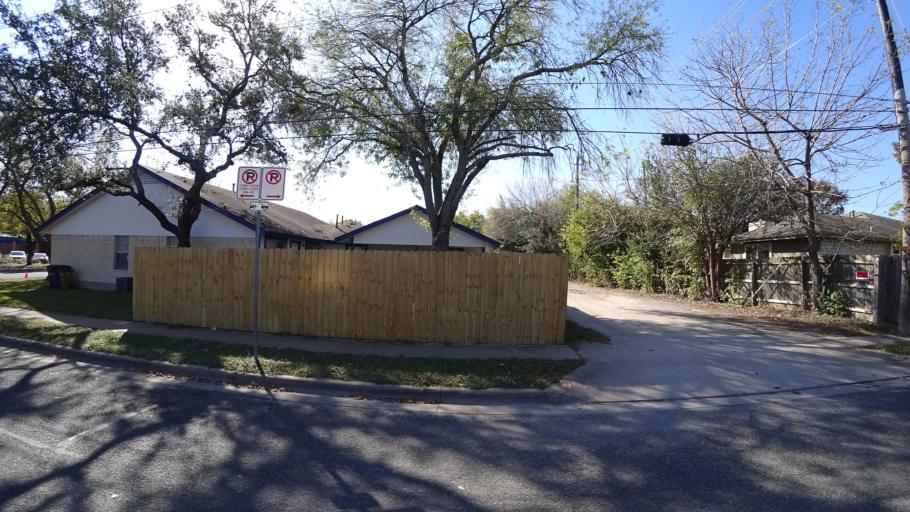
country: US
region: Texas
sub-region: Travis County
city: Barton Creek
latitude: 30.2328
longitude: -97.8463
